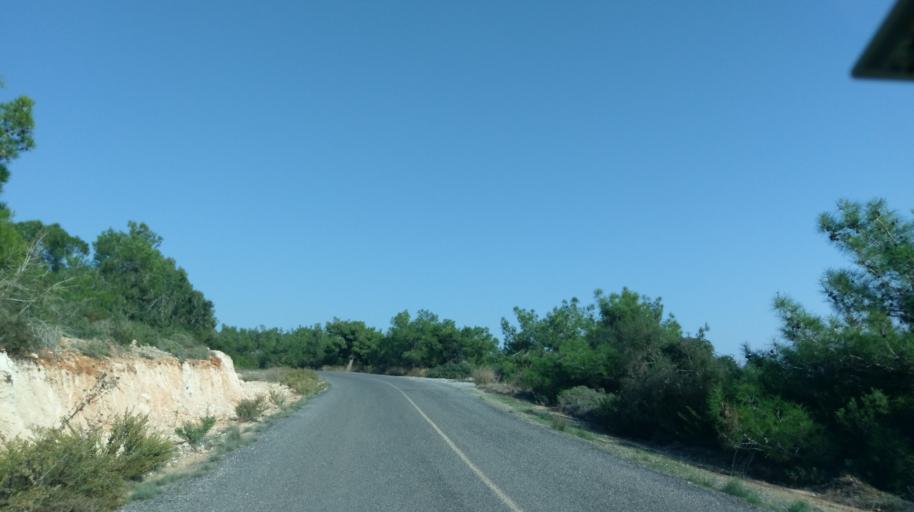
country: CY
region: Ammochostos
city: Leonarisso
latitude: 35.4877
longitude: 34.1874
